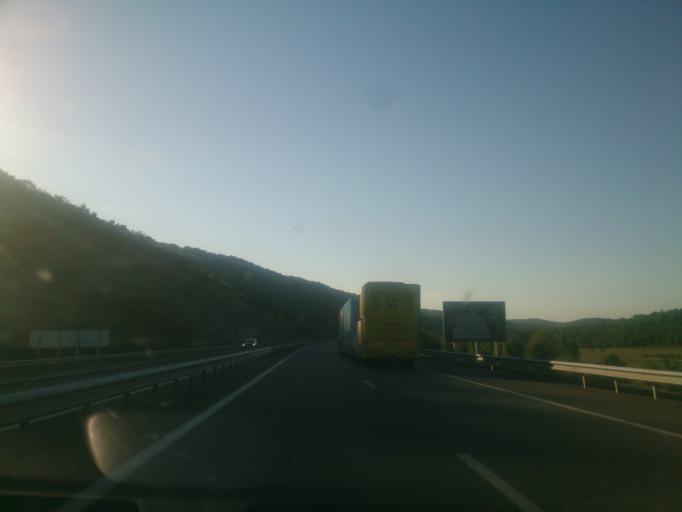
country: FR
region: Midi-Pyrenees
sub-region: Departement du Lot
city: Le Vigan
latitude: 44.7946
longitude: 1.5171
